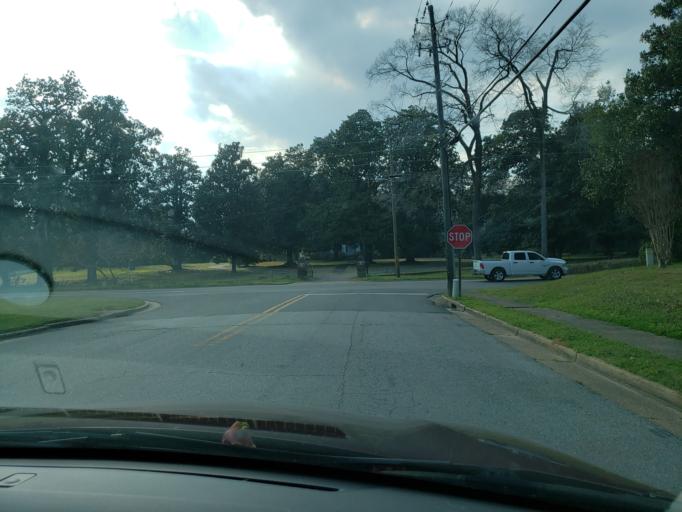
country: US
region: Alabama
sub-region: Hale County
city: Greensboro
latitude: 32.7042
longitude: -87.6065
